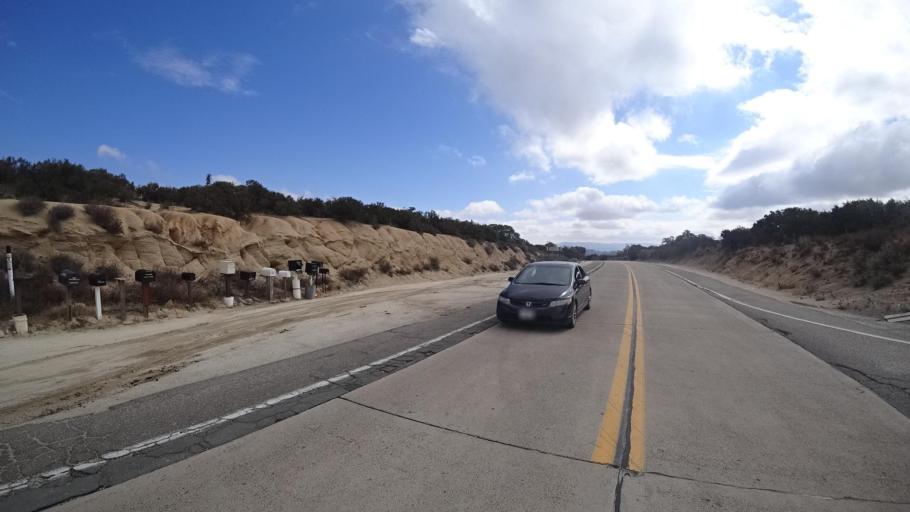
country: US
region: California
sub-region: San Diego County
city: Campo
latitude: 32.6699
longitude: -116.3152
